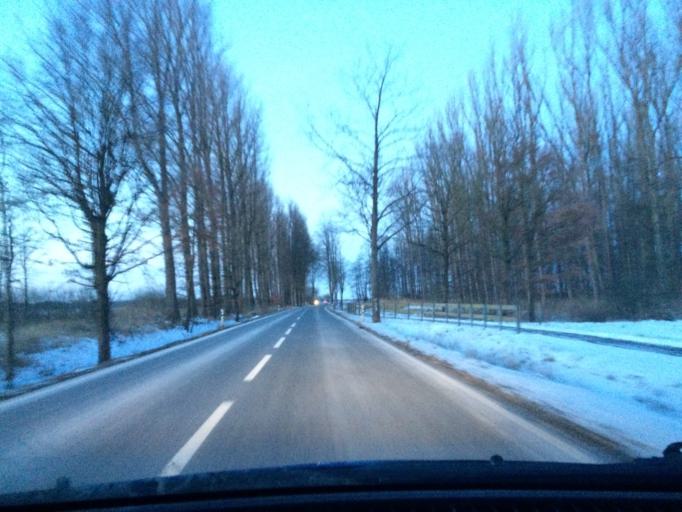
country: DE
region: Lower Saxony
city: Marschacht
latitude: 53.4082
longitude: 10.3604
